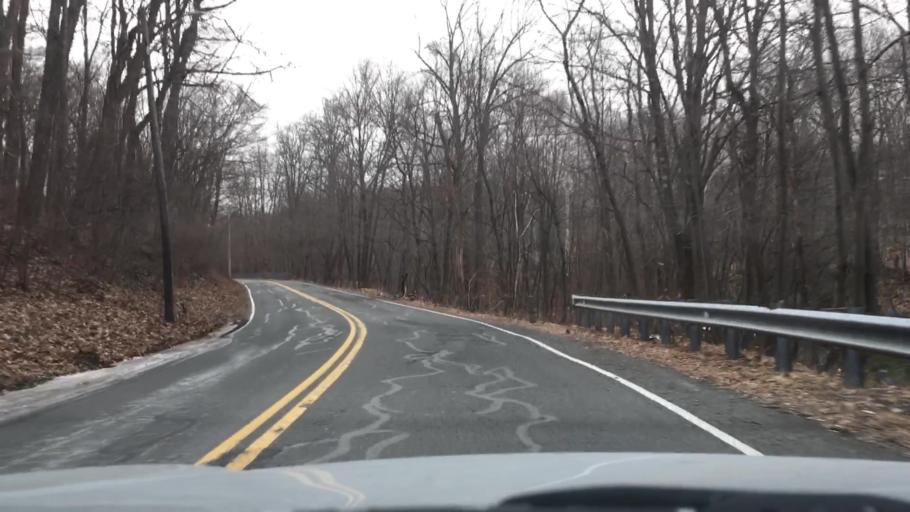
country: US
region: Massachusetts
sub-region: Hampshire County
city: Northampton
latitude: 42.3244
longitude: -72.6674
